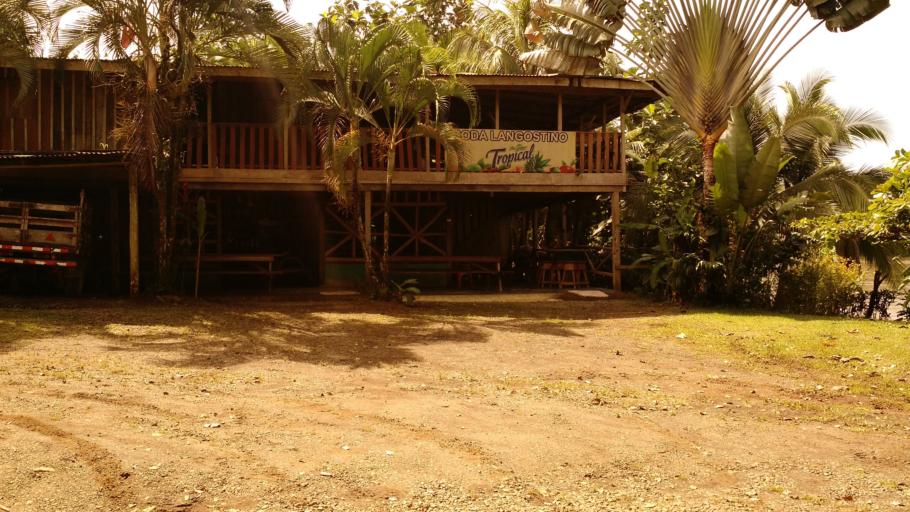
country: CR
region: Alajuela
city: Pital
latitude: 10.7840
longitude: -84.1956
